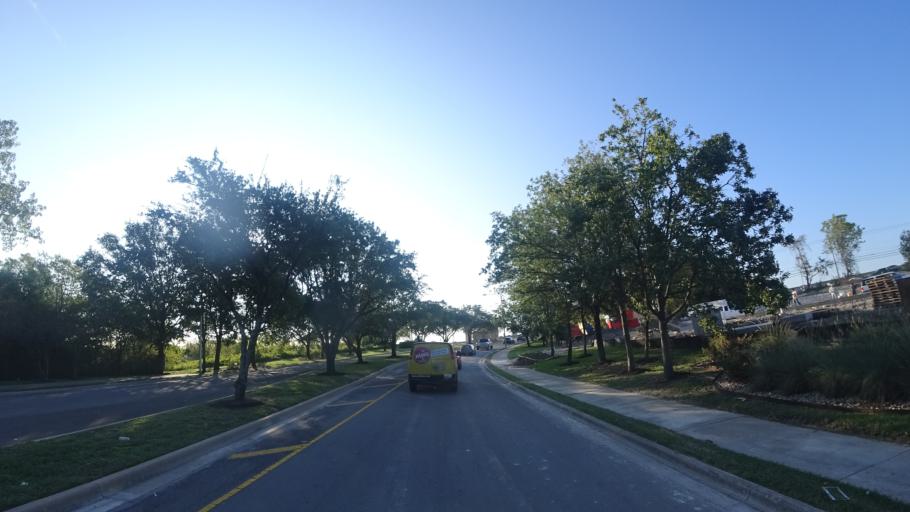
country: US
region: Texas
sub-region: Travis County
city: Austin
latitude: 30.3290
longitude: -97.6665
